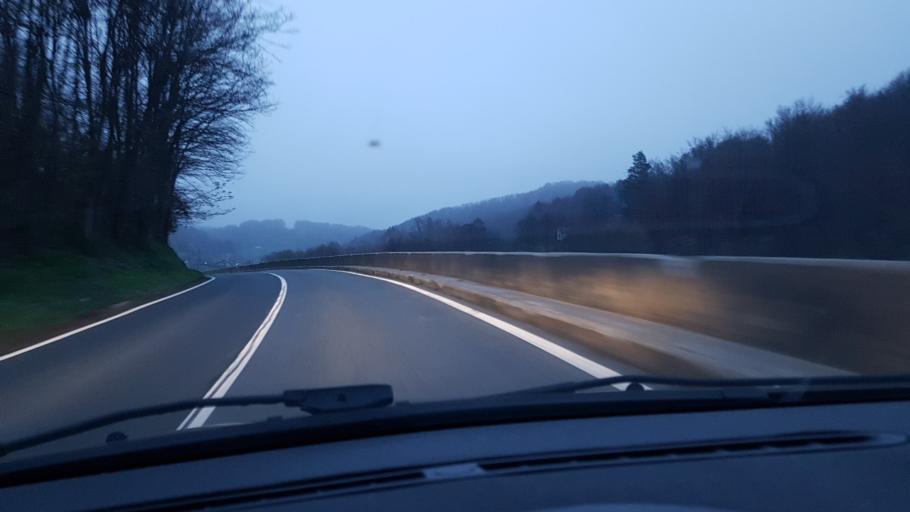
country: HR
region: Krapinsko-Zagorska
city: Pregrada
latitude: 46.2087
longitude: 15.7942
